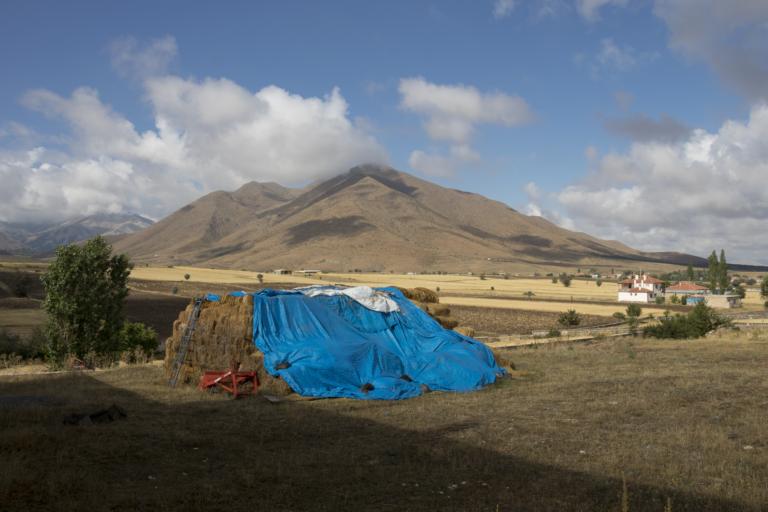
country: TR
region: Kayseri
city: Toklar
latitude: 38.4066
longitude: 36.0801
